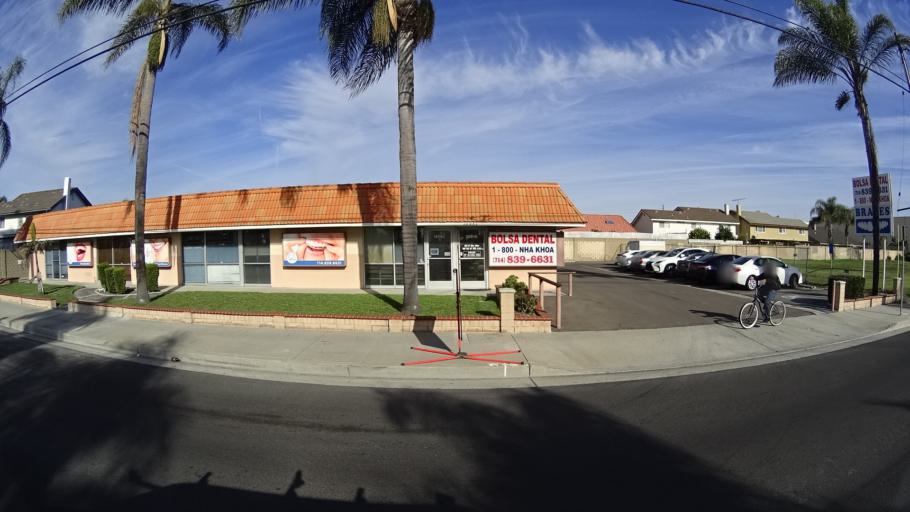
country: US
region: California
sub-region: Orange County
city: Garden Grove
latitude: 33.7451
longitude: -117.9536
